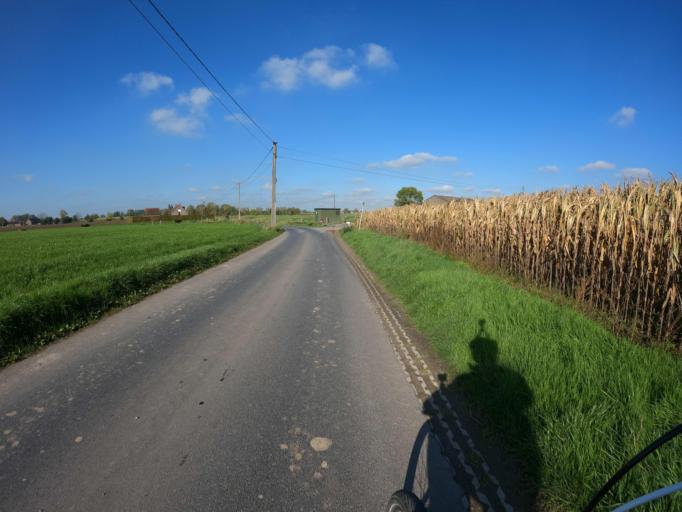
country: BE
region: Flanders
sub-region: Provincie West-Vlaanderen
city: Ruiselede
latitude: 51.0363
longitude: 3.3727
